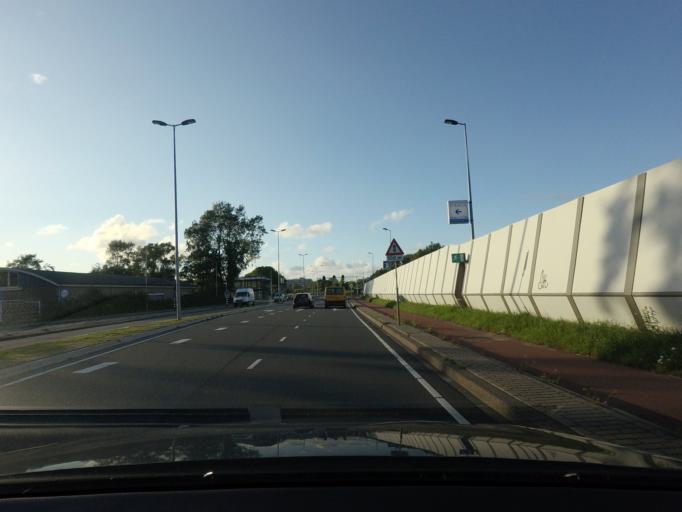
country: NL
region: North Holland
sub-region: Gemeente Alkmaar
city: Alkmaar
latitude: 52.6257
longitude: 4.7738
